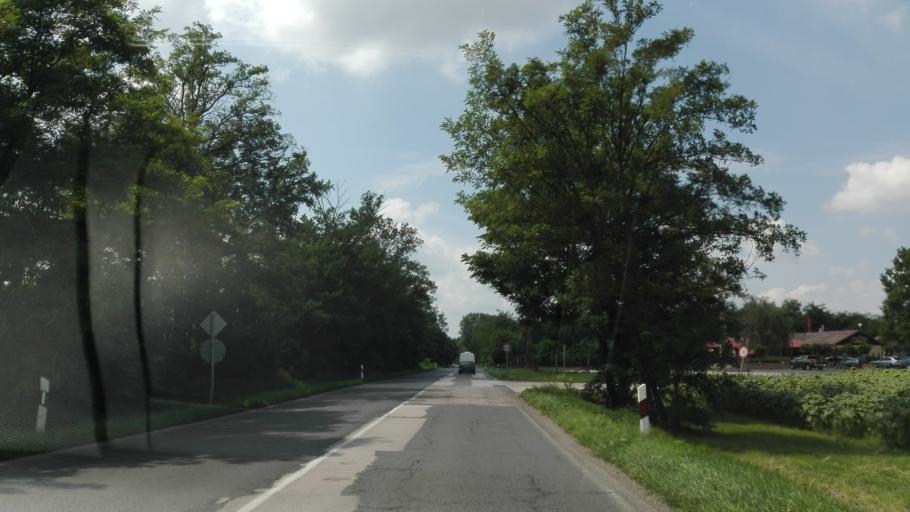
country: HU
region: Fejer
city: Cece
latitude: 46.7743
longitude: 18.6616
